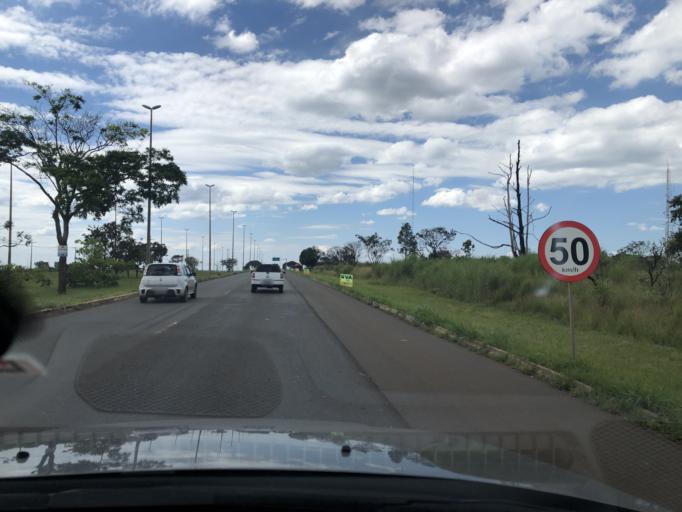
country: BR
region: Federal District
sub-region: Brasilia
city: Brasilia
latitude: -15.9777
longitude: -47.9946
